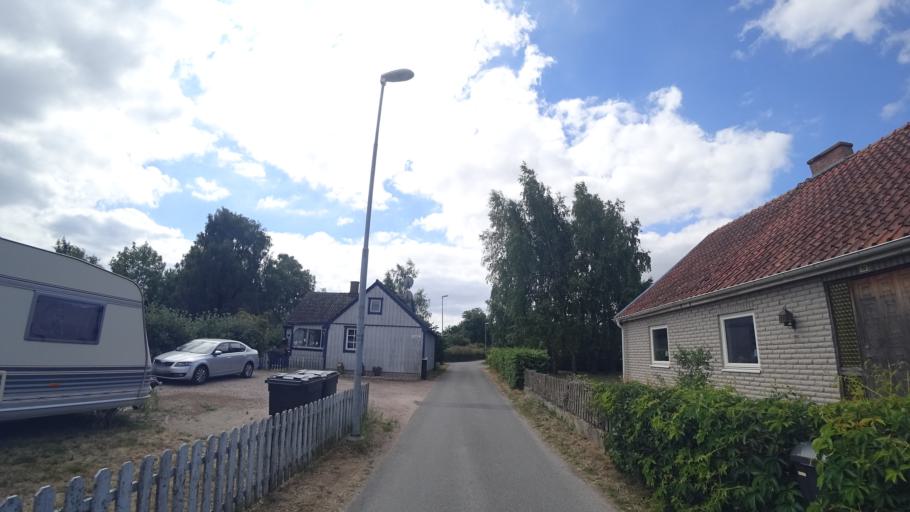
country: SE
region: Skane
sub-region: Kristianstads Kommun
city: Fjalkinge
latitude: 55.9890
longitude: 14.2694
